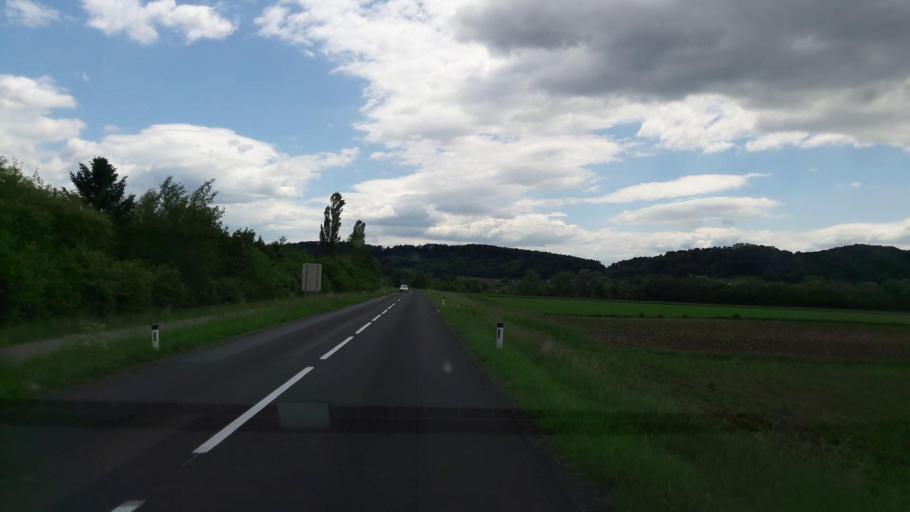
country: AT
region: Styria
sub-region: Politischer Bezirk Hartberg-Fuerstenfeld
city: Soechau
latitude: 47.0716
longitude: 16.0006
